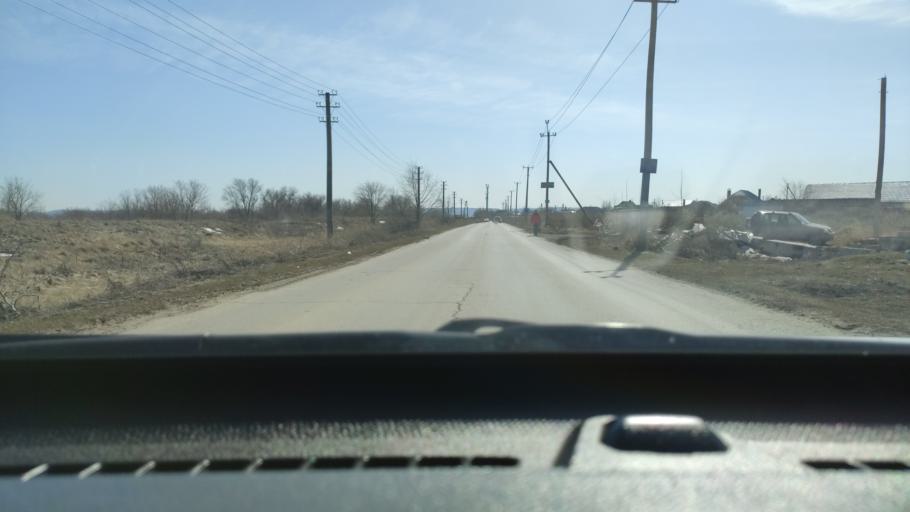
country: RU
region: Samara
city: Podstepki
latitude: 53.5132
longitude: 49.1926
